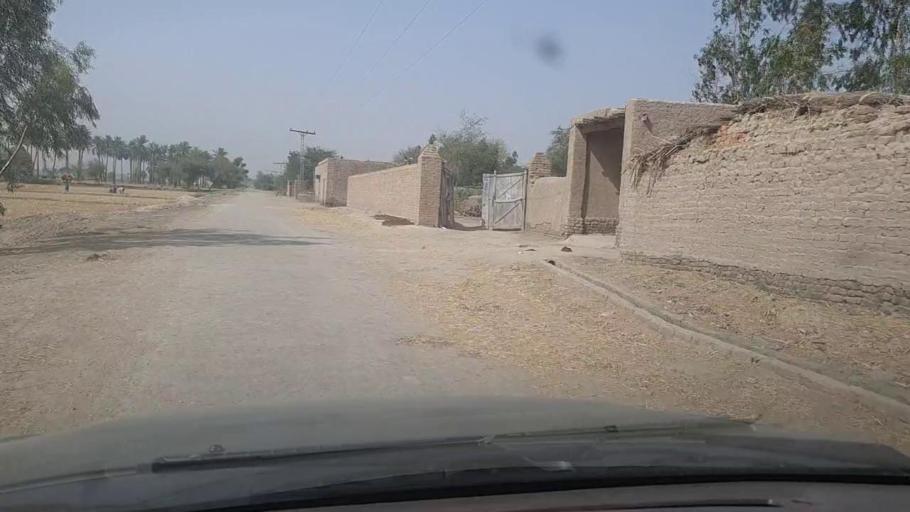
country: PK
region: Sindh
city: Garhi Yasin
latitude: 27.8735
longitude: 68.5606
